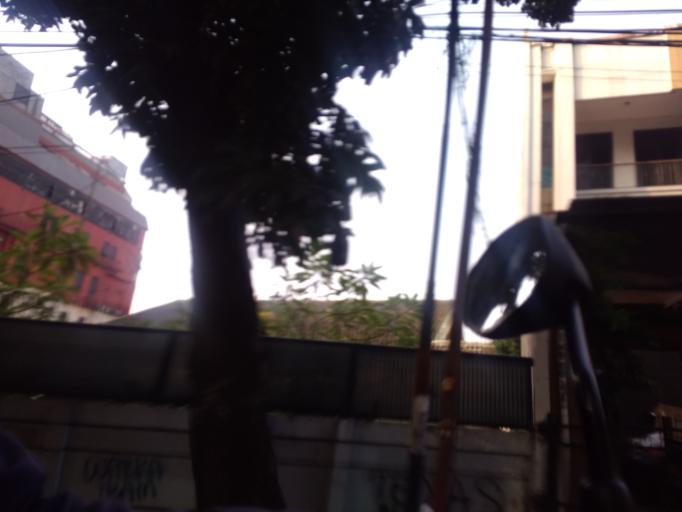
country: ID
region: Jakarta Raya
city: Jakarta
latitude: -6.2658
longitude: 106.7987
